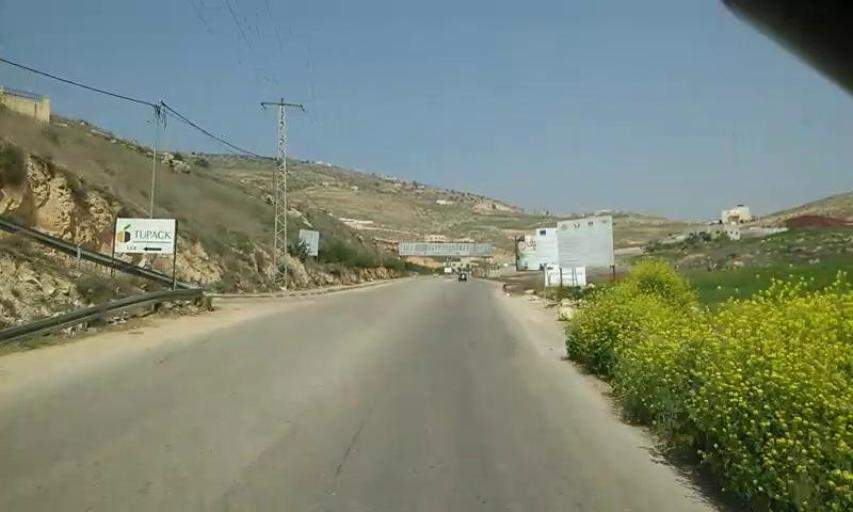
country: PS
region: West Bank
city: Tubas
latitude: 32.3037
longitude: 35.3638
